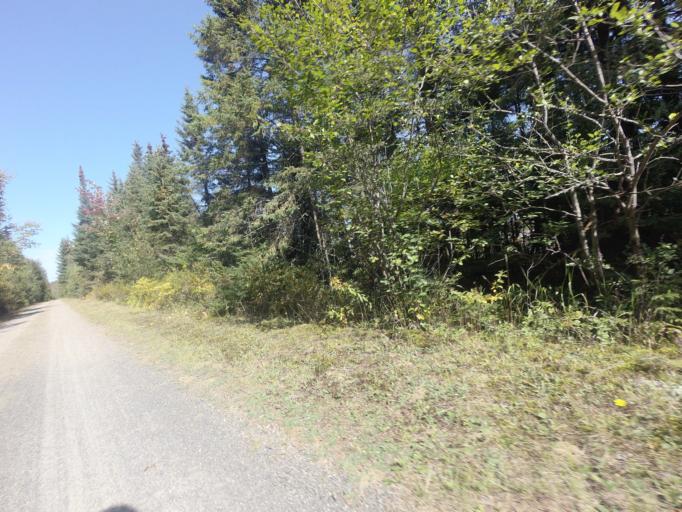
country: CA
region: Quebec
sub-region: Laurentides
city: Sainte-Agathe-des-Monts
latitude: 46.0698
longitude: -74.3143
